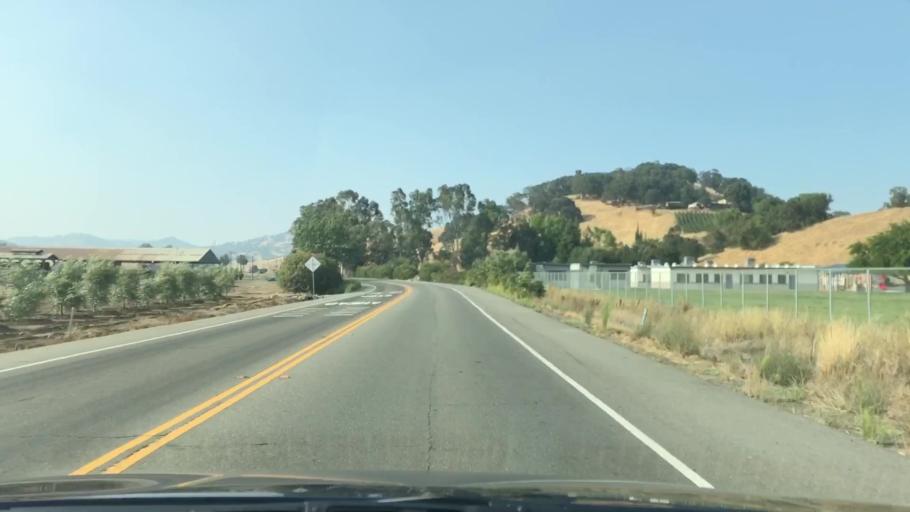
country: US
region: California
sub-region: Solano County
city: Green Valley
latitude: 38.2878
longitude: -122.1182
